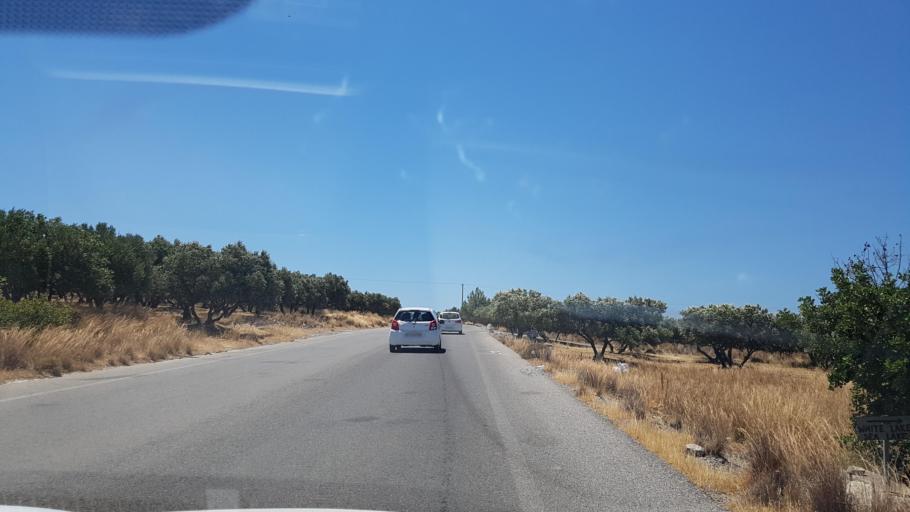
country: GR
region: Crete
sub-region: Nomos Chanias
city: Vryses
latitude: 35.3050
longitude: 23.5376
